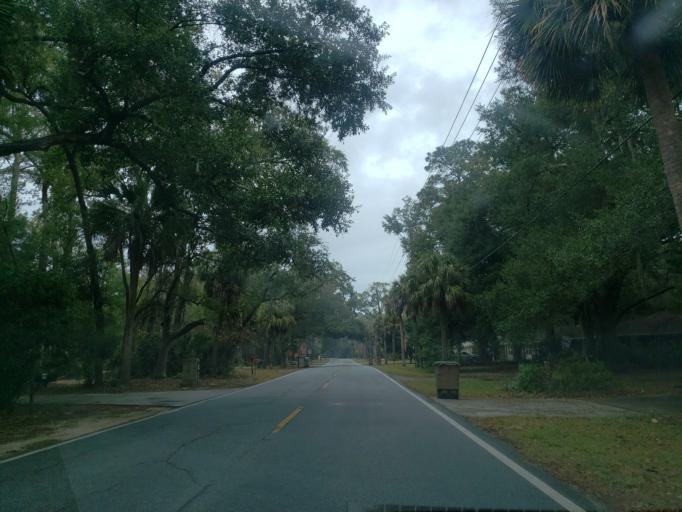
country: US
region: Georgia
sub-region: Chatham County
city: Wilmington Island
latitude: 31.9912
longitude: -80.9945
